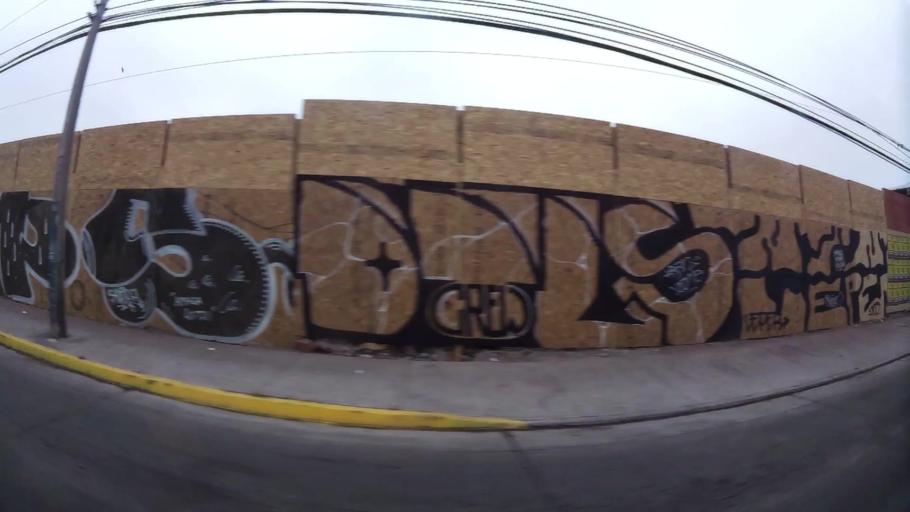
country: CL
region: Santiago Metropolitan
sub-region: Provincia de Santiago
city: Santiago
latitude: -33.4892
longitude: -70.6408
